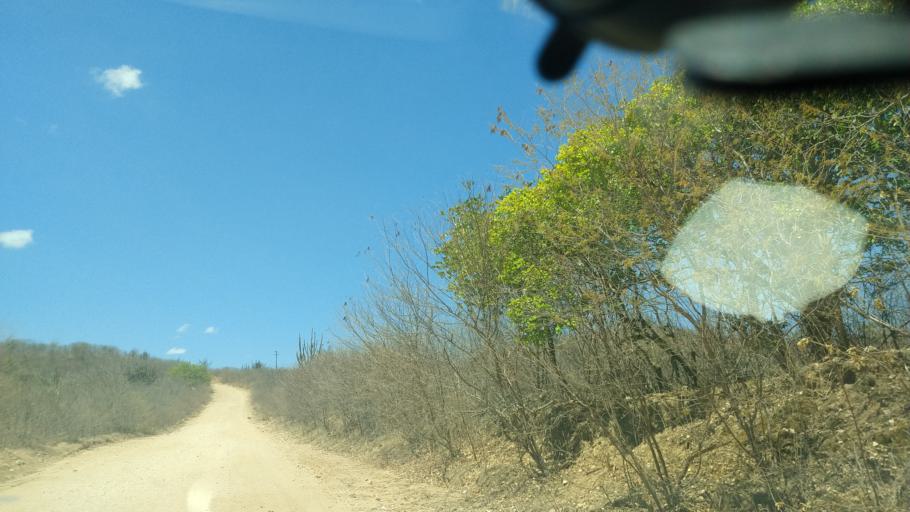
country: BR
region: Rio Grande do Norte
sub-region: Cerro Cora
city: Cerro Cora
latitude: -6.0116
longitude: -36.2988
